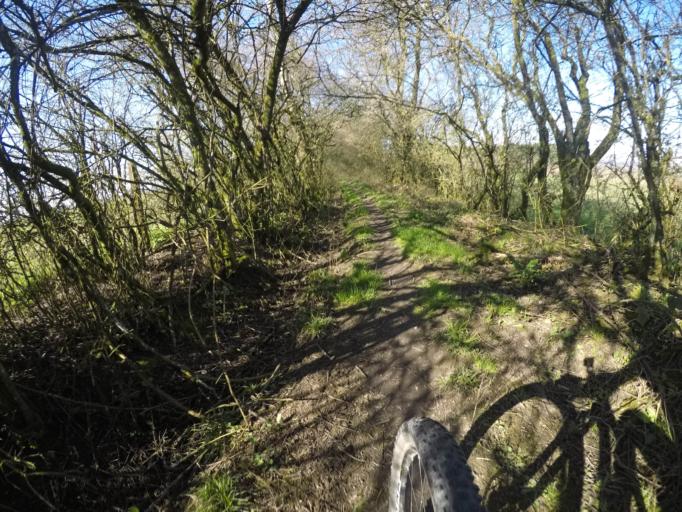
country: BE
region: Wallonia
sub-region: Province du Luxembourg
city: Tintigny
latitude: 49.7057
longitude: 5.5518
